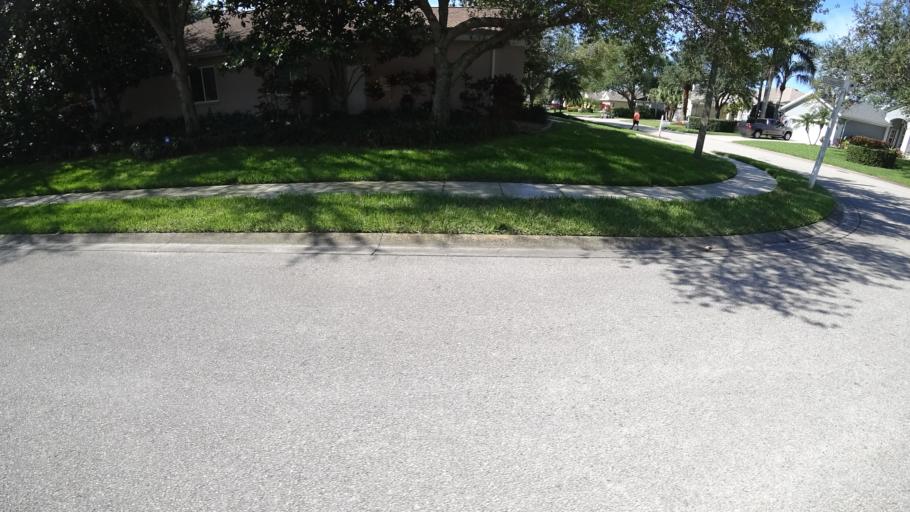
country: US
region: Florida
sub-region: Manatee County
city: West Bradenton
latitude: 27.5104
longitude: -82.6551
